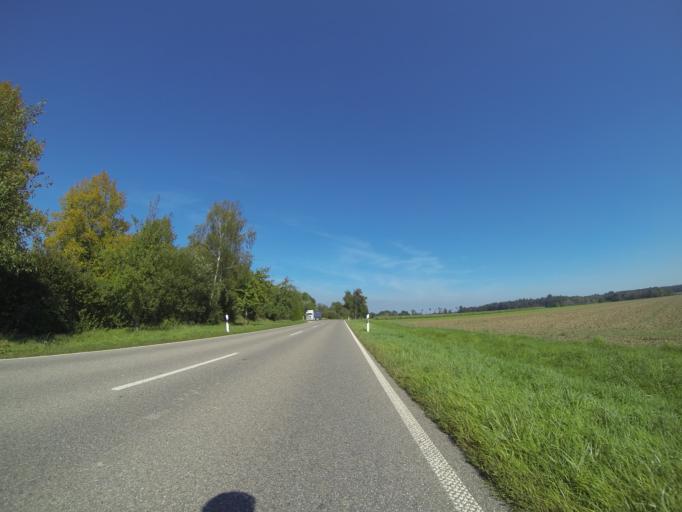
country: DE
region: Baden-Wuerttemberg
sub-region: Tuebingen Region
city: Erbach
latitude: 48.3094
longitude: 9.9101
